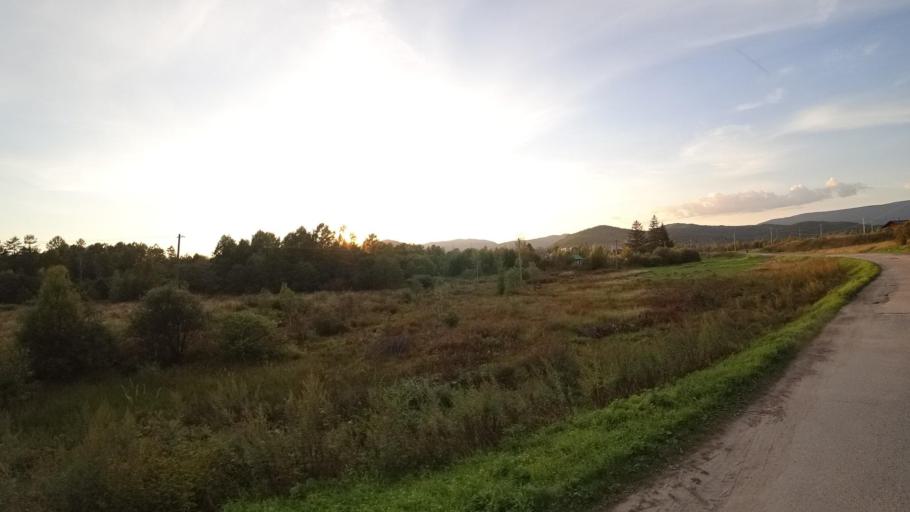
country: RU
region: Jewish Autonomous Oblast
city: Kul'dur
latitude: 49.1973
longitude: 131.6336
